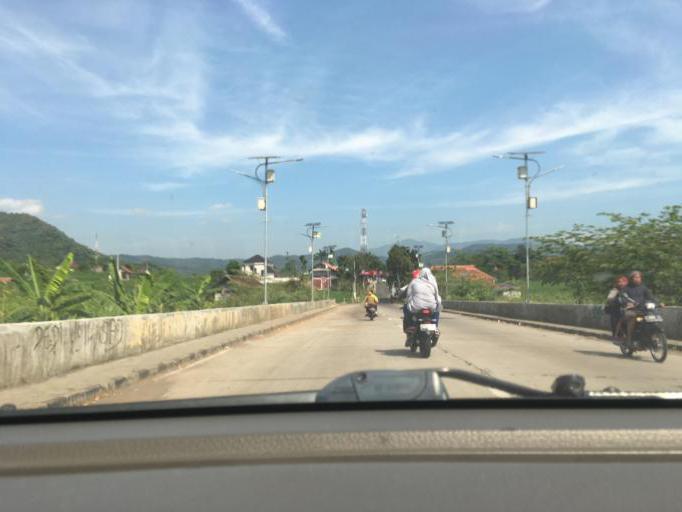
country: ID
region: West Java
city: Cilengkrang
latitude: -6.9455
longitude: 108.1005
